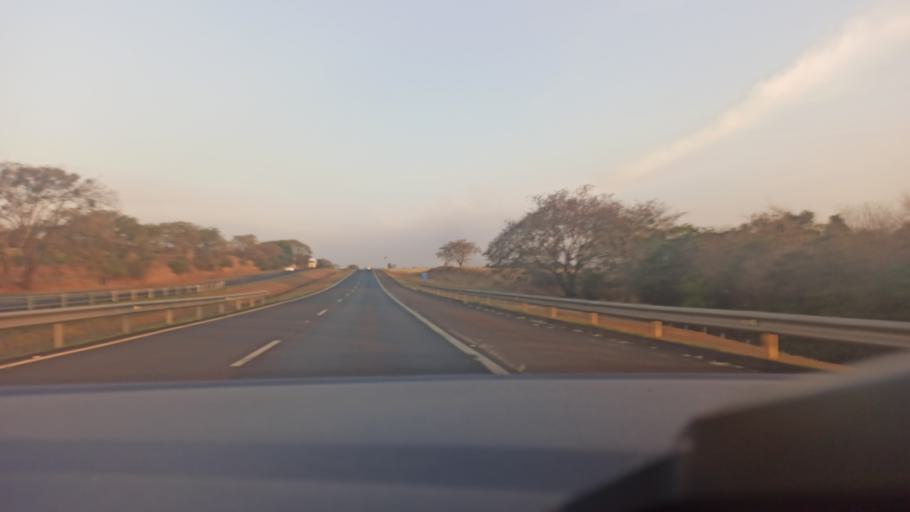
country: BR
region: Sao Paulo
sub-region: Taquaritinga
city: Taquaritinga
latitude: -21.4288
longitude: -48.6664
